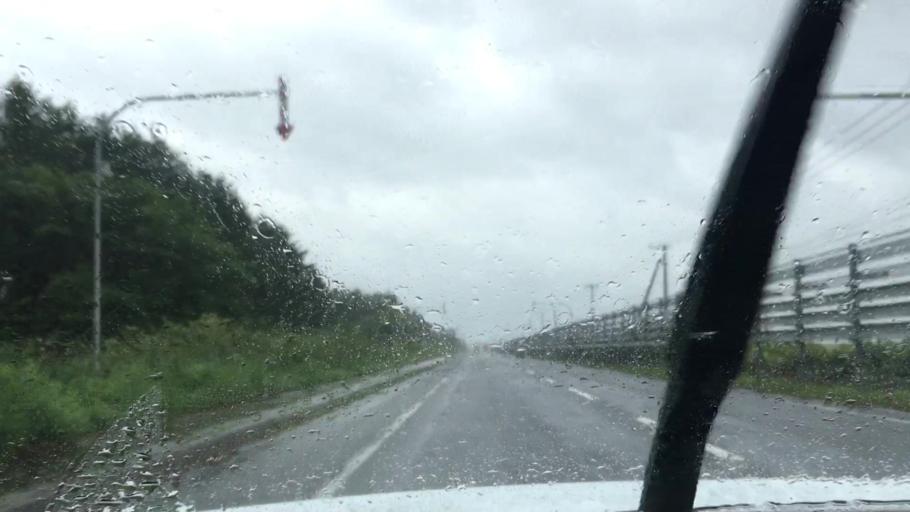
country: JP
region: Hokkaido
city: Nanae
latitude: 42.3113
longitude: 140.2732
